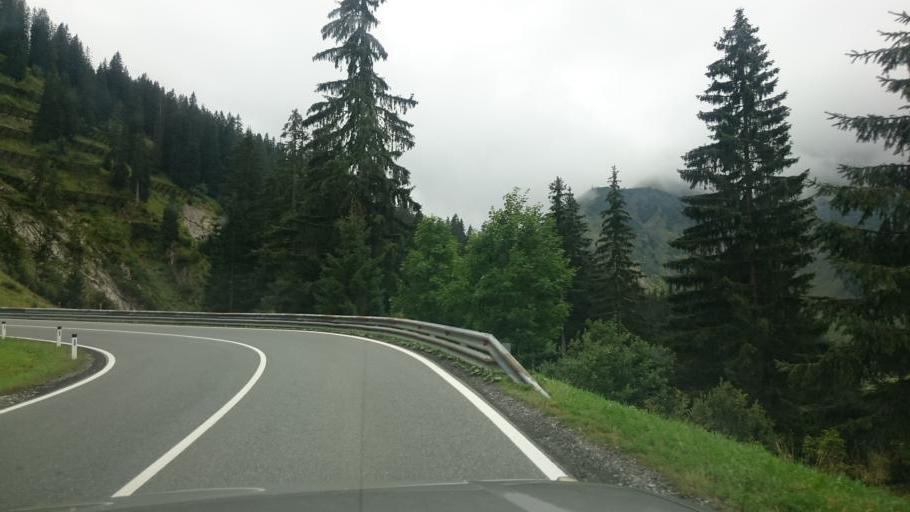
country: AT
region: Vorarlberg
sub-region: Politischer Bezirk Bregenz
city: Schroecken
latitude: 47.2576
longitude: 10.0996
